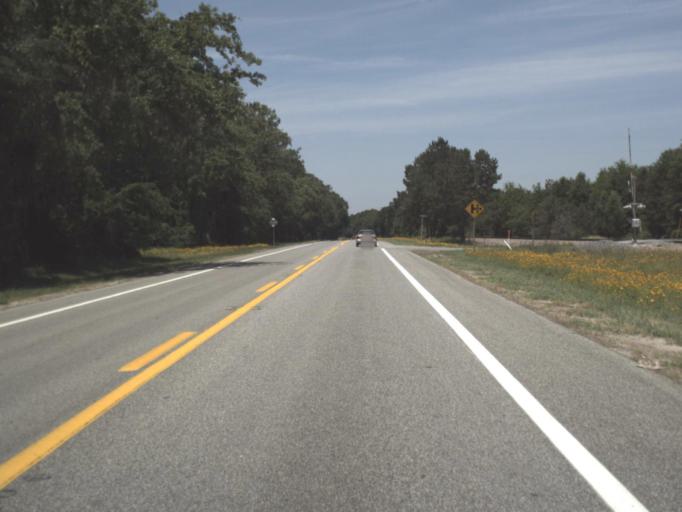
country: US
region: Florida
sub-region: Suwannee County
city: Live Oak
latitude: 30.3679
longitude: -83.1441
